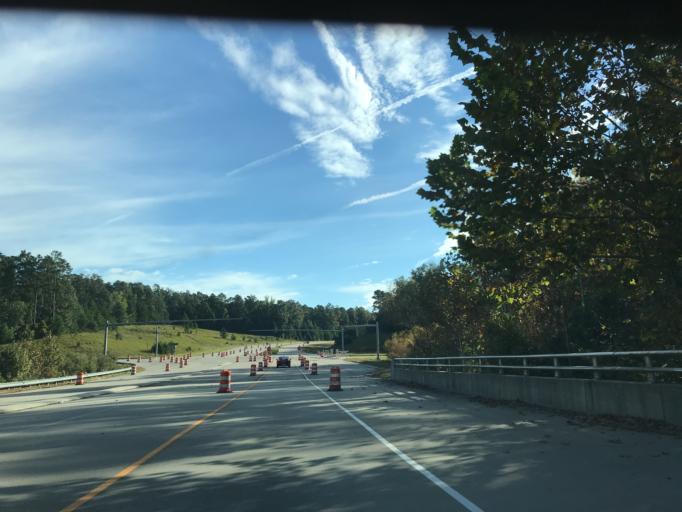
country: US
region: North Carolina
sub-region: Wake County
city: Morrisville
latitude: 35.8469
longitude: -78.8817
